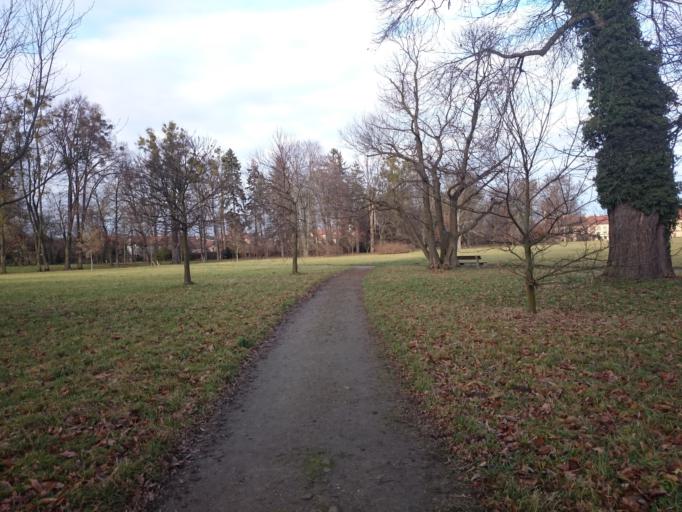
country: CZ
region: Pardubicky
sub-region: Okres Chrudim
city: Hermanuv Mestec
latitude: 49.9427
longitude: 15.6668
